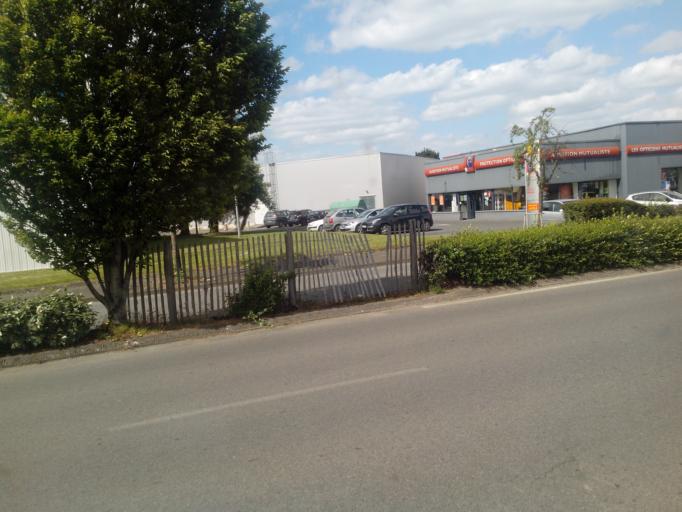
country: FR
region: Brittany
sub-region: Departement des Cotes-d'Armor
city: Langueux
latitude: 48.4965
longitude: -2.7260
